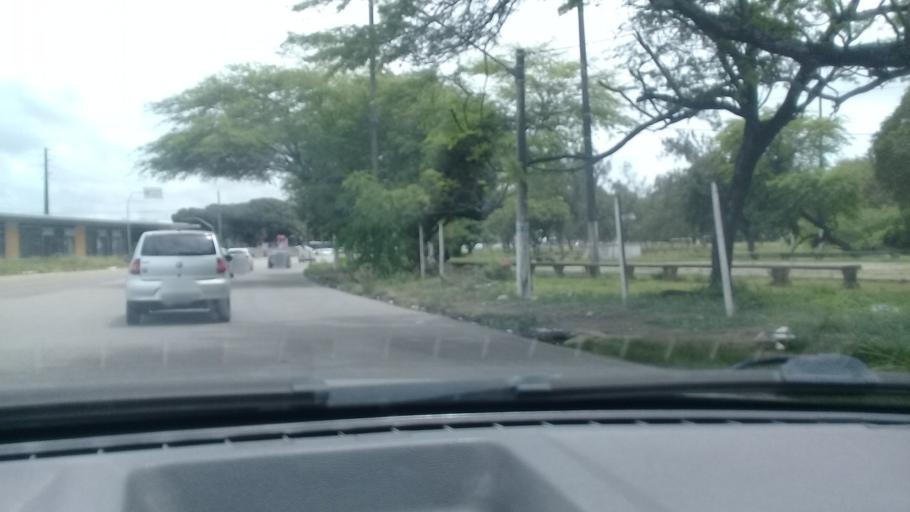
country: BR
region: Pernambuco
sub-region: Olinda
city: Olinda
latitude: -8.0281
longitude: -34.8647
